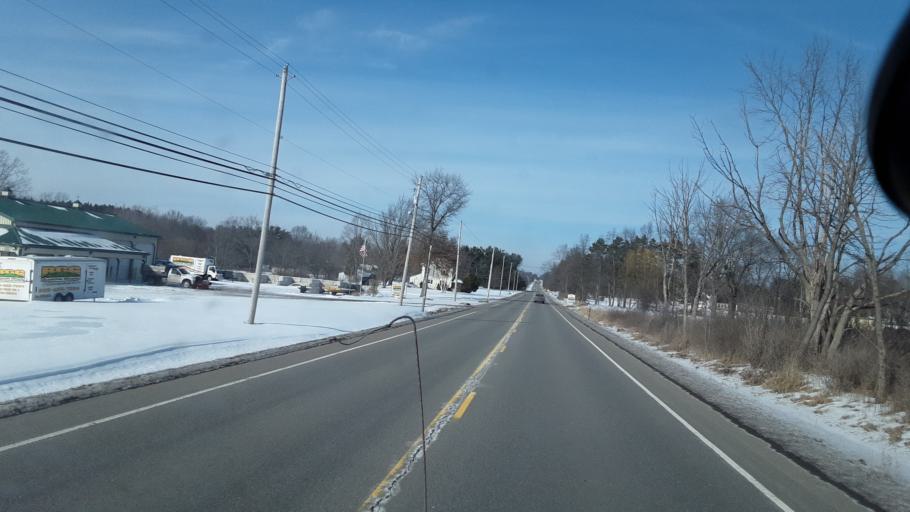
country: US
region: Ohio
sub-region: Mahoning County
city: Canfield
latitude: 40.9966
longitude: -80.7607
